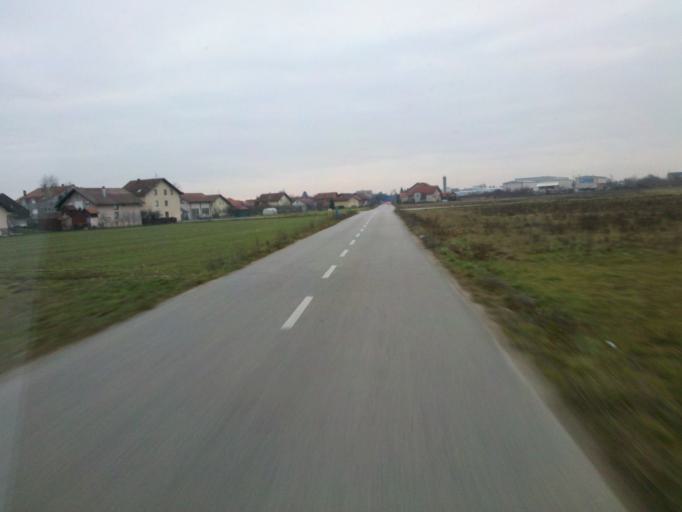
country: HR
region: Grad Zagreb
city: Lucko
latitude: 45.7580
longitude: 15.8726
